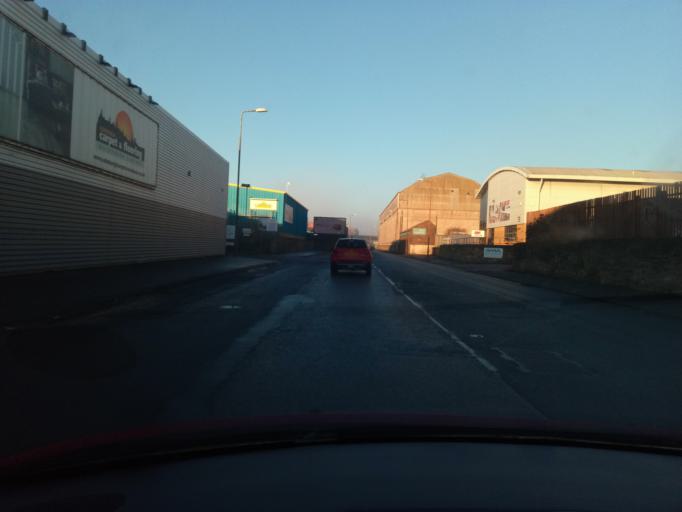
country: GB
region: Scotland
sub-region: West Lothian
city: Seafield
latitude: 55.9720
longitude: -3.1536
